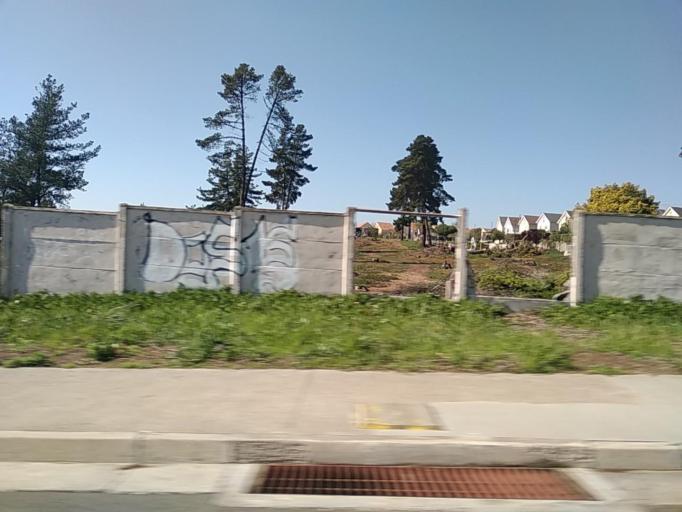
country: CL
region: Valparaiso
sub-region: Provincia de Valparaiso
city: Vina del Mar
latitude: -32.9402
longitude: -71.5370
